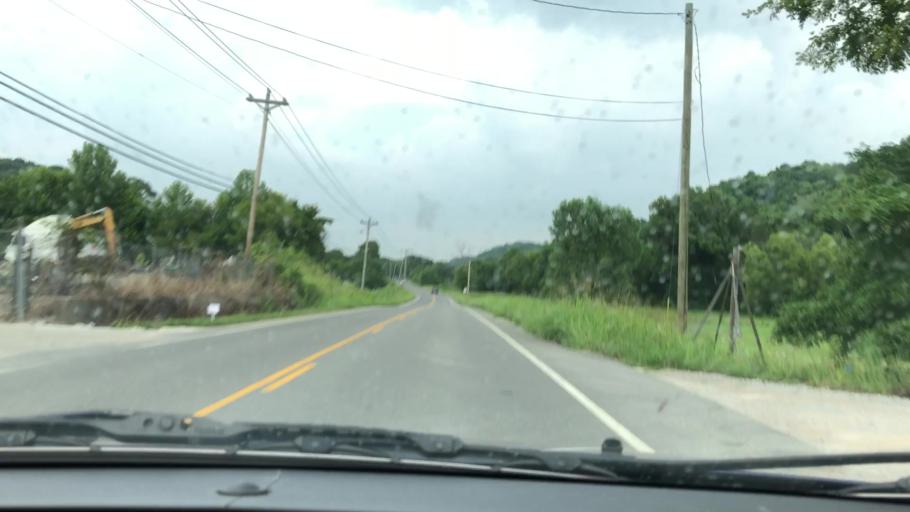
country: US
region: Tennessee
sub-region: Williamson County
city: Franklin
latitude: 35.8935
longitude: -86.9233
